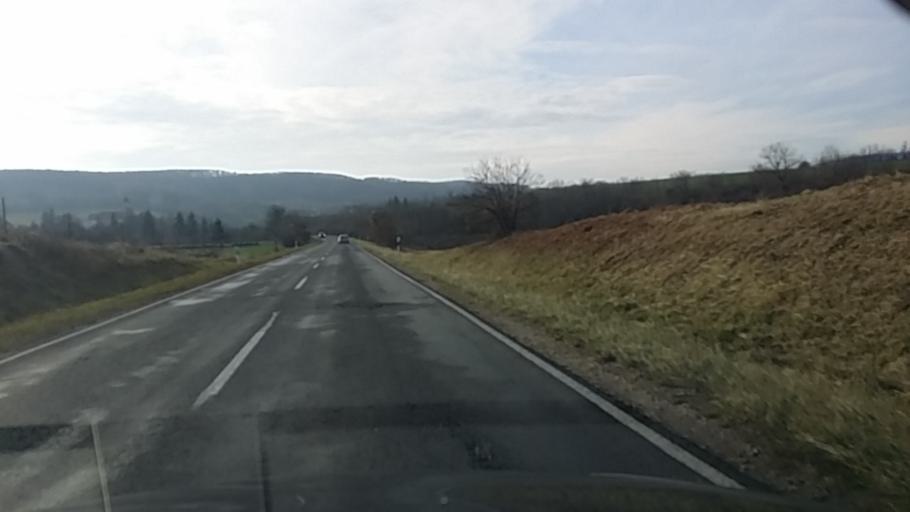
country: HU
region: Veszprem
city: Zanka
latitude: 46.9674
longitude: 17.6260
